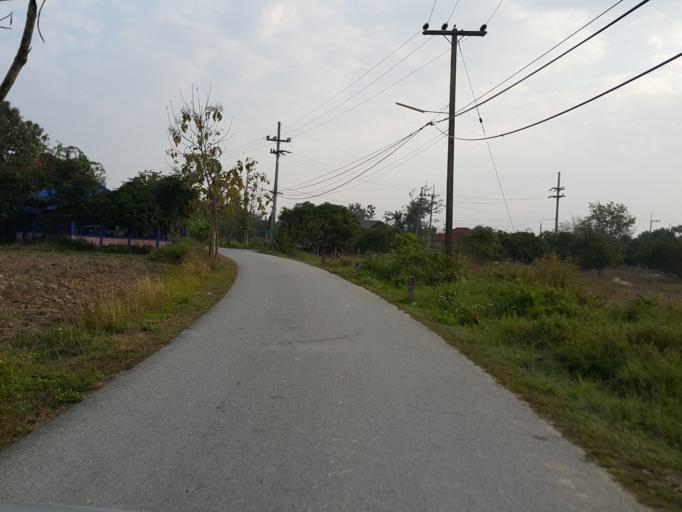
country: TH
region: Chiang Mai
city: San Sai
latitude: 18.8172
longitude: 99.1008
